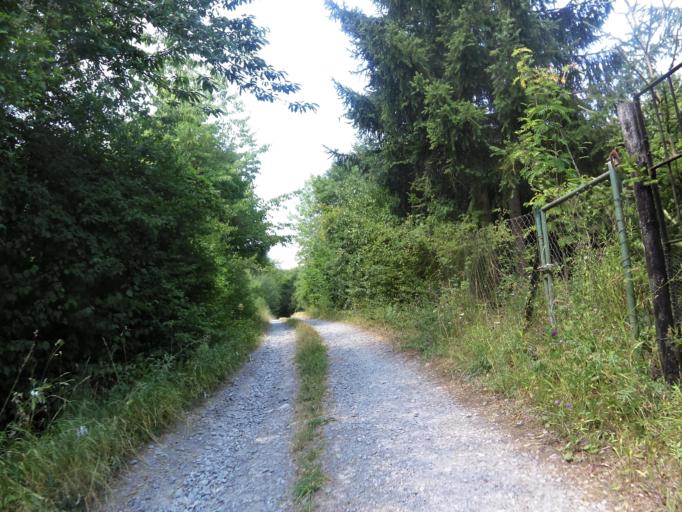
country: DE
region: Bavaria
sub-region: Regierungsbezirk Unterfranken
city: Wuerzburg
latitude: 49.8152
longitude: 9.9488
